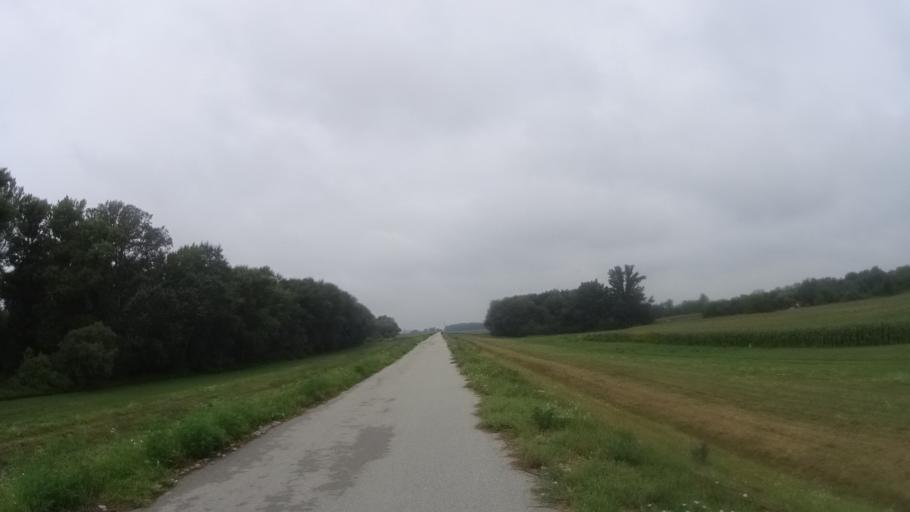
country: HU
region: Komarom-Esztergom
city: Almasfuzito
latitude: 47.7458
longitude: 18.2253
